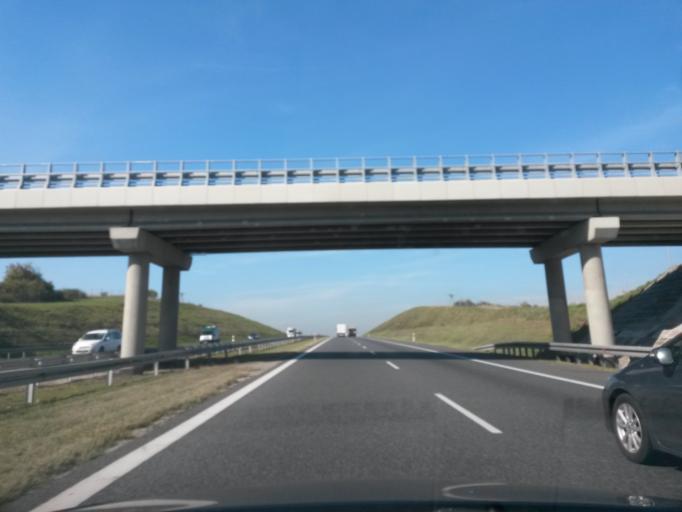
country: PL
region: Silesian Voivodeship
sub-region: Powiat bierunsko-ledzinski
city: Imielin
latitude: 50.1628
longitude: 19.2239
